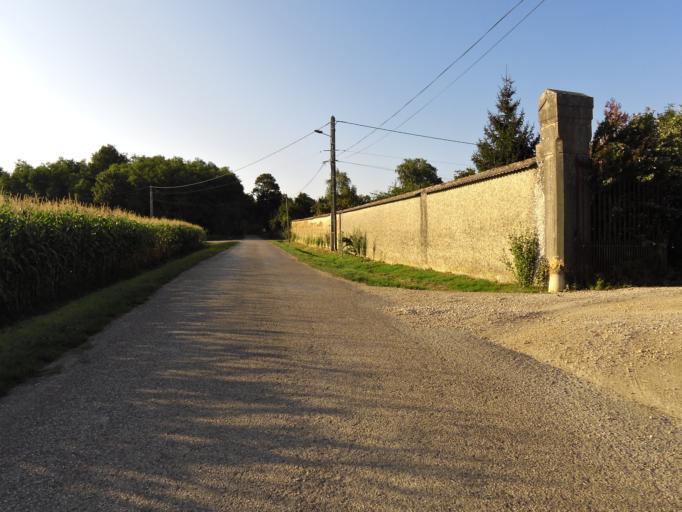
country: FR
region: Rhone-Alpes
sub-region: Departement de l'Ain
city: Perouges
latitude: 45.9343
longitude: 5.1700
